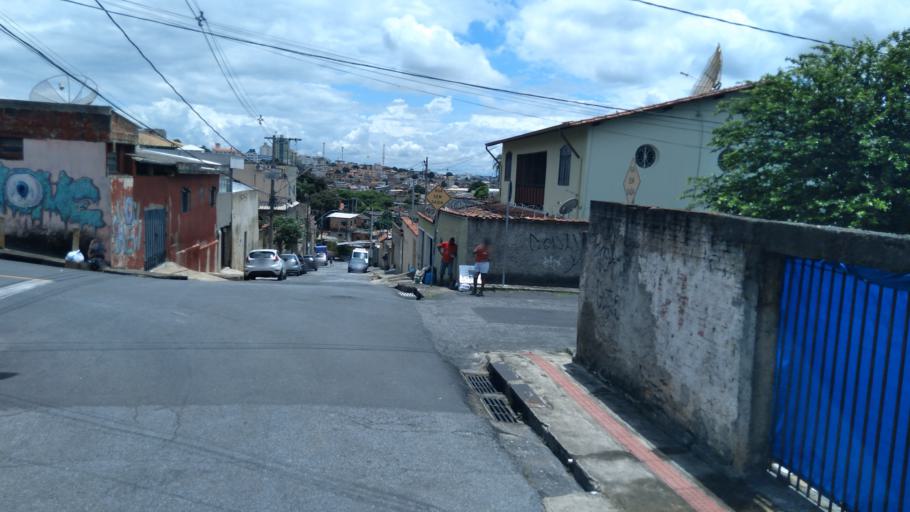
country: BR
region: Minas Gerais
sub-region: Belo Horizonte
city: Belo Horizonte
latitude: -19.9200
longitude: -43.9020
